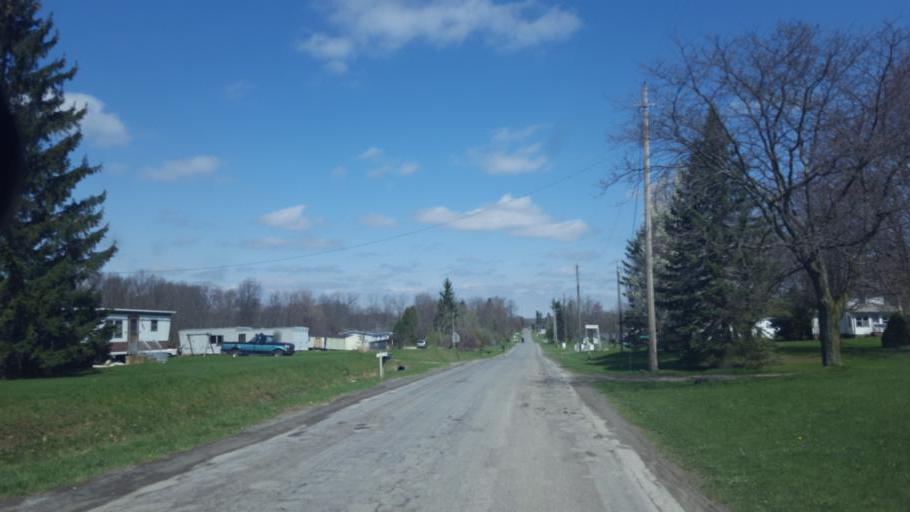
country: US
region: Ohio
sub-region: Geauga County
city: Middlefield
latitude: 41.4418
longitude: -81.0806
